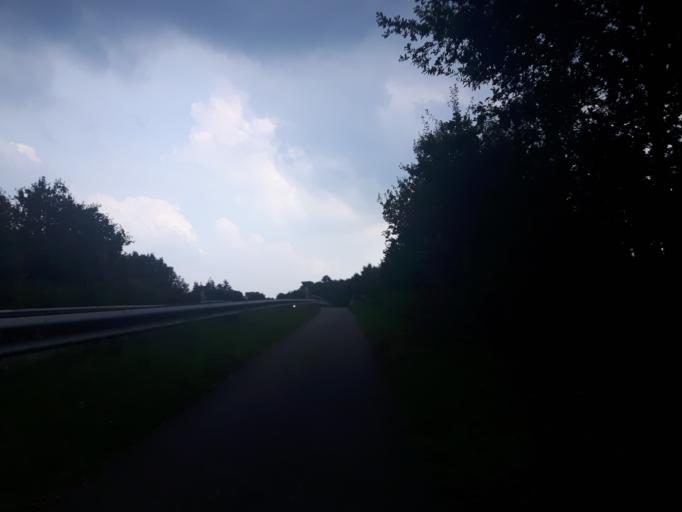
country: NL
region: Overijssel
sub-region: Gemeente Hengelo
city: Hengelo
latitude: 52.2836
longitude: 6.8546
